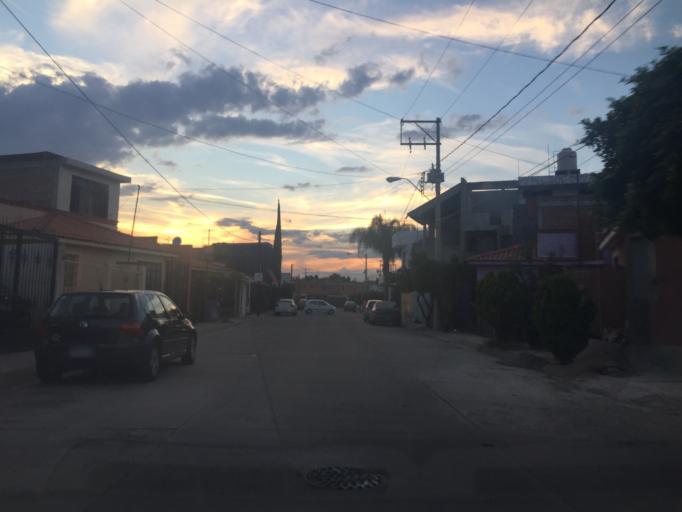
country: MX
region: Guanajuato
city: Leon
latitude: 21.1524
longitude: -101.6551
